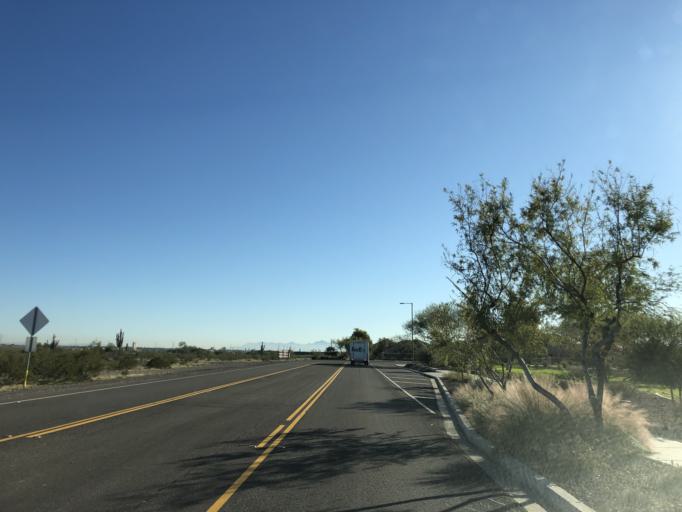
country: US
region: Arizona
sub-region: Maricopa County
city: Sun City West
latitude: 33.6905
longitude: -112.3124
